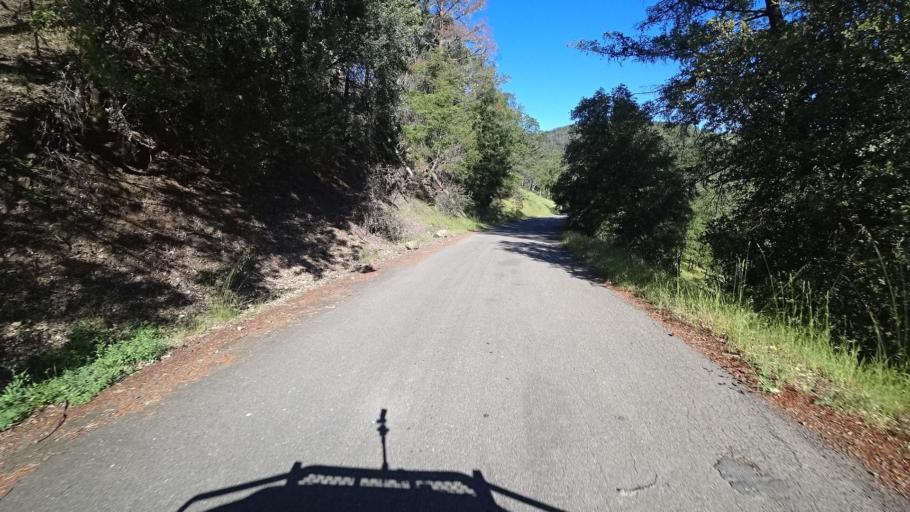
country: US
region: California
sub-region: Lake County
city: Upper Lake
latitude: 39.4082
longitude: -122.9766
